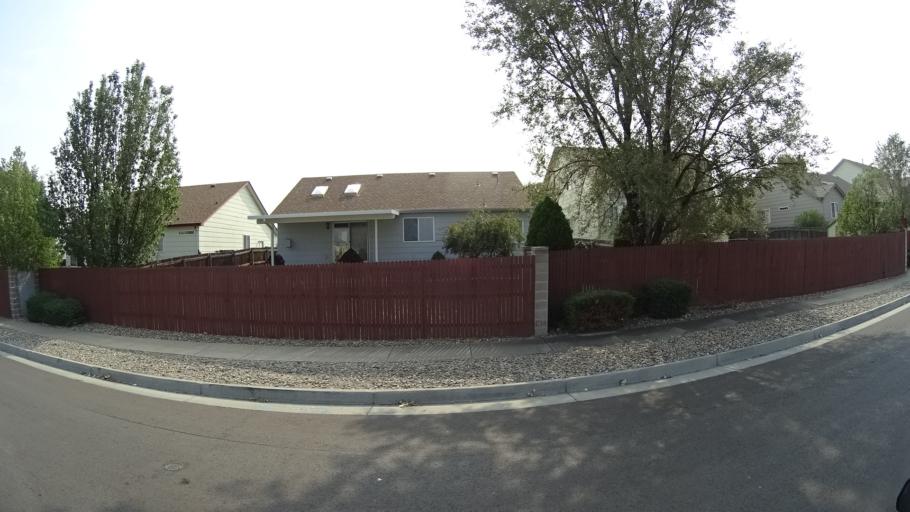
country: US
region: Colorado
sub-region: El Paso County
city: Stratmoor
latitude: 38.8199
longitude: -104.7533
